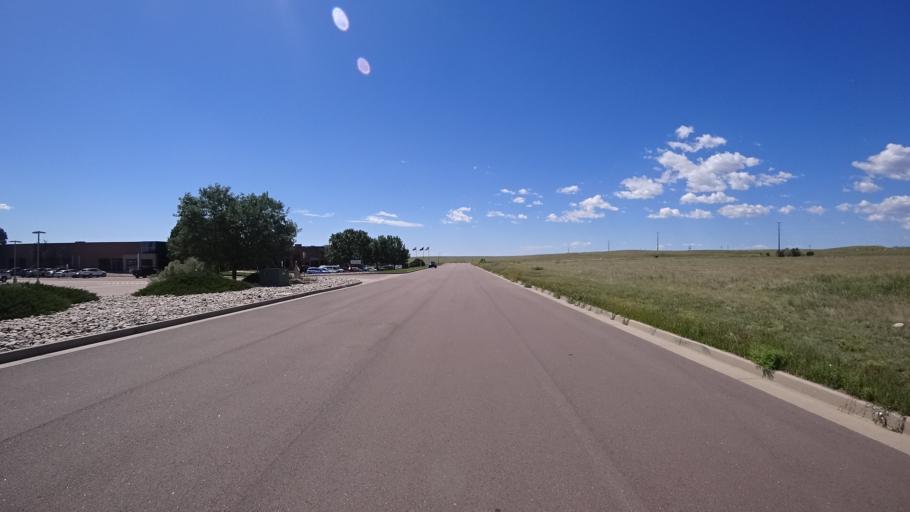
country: US
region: Colorado
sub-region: El Paso County
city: Security-Widefield
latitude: 38.7661
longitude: -104.6693
